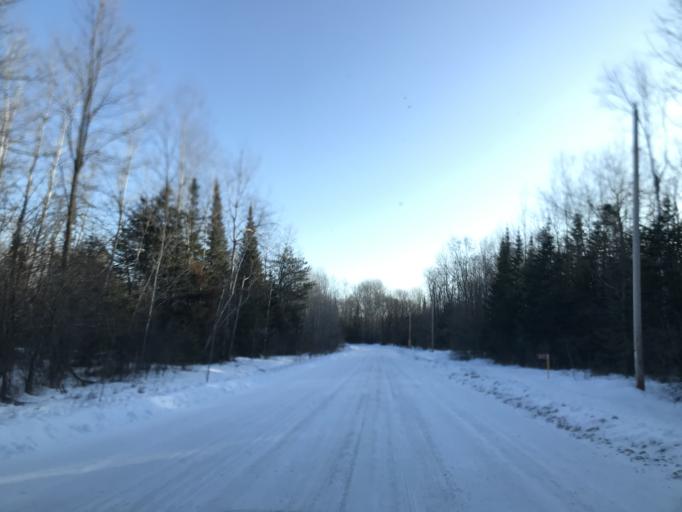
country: US
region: Michigan
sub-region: Menominee County
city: Menominee
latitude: 45.2904
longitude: -87.6978
